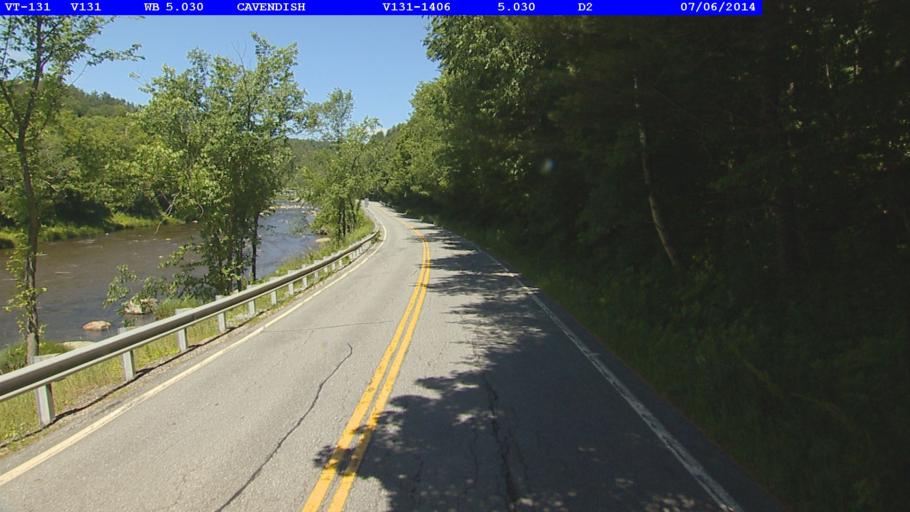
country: US
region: Vermont
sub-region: Windsor County
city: Springfield
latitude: 43.4028
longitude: -72.5713
